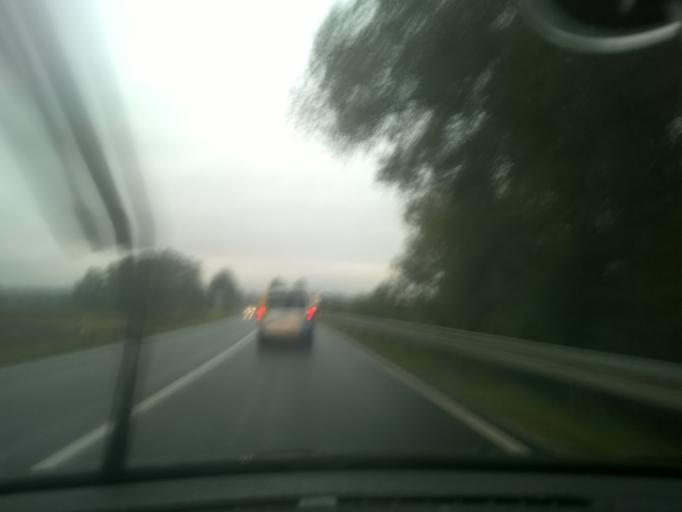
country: HR
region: Zagrebacka
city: Pojatno
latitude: 45.9291
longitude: 15.8206
